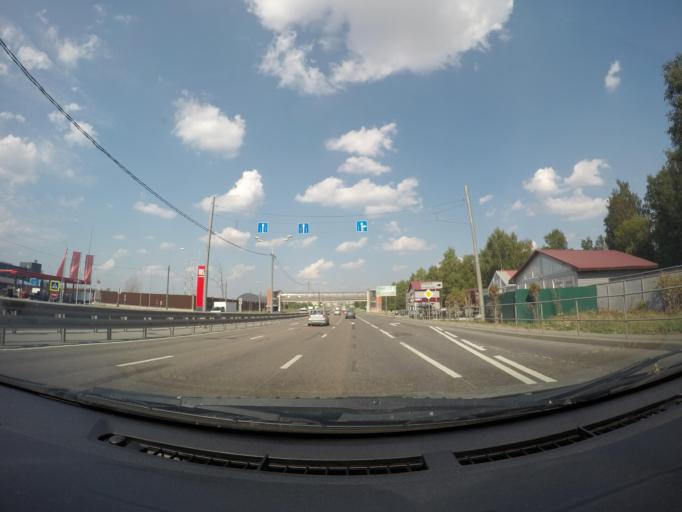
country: RU
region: Moscow
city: Businovo
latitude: 55.9065
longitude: 37.4934
